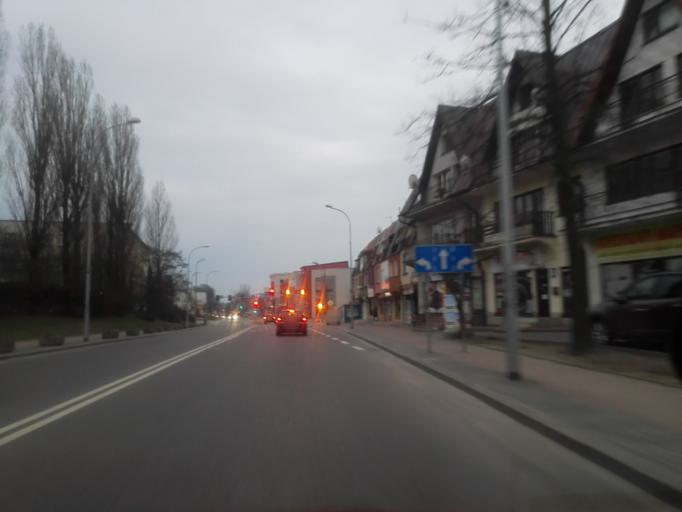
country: PL
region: Podlasie
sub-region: Lomza
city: Lomza
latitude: 53.1790
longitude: 22.0743
